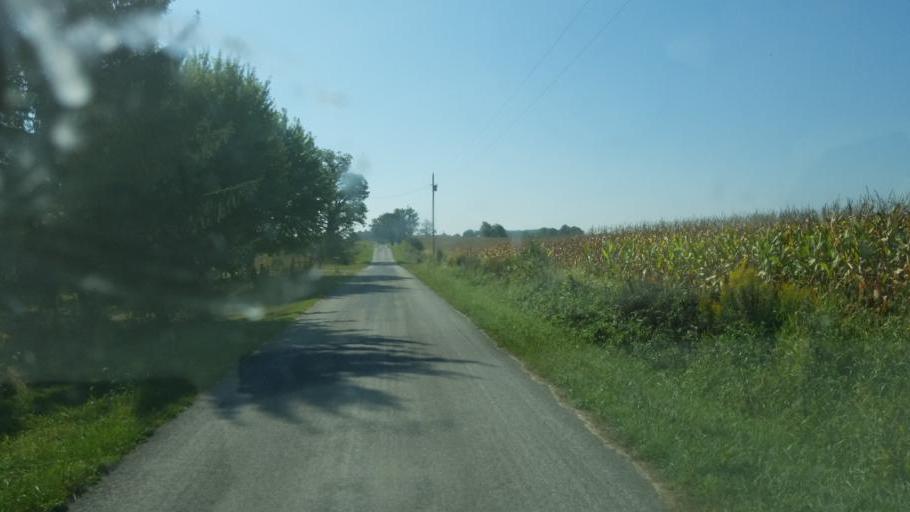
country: US
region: Ohio
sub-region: Union County
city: Richwood
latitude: 40.5135
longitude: -83.4077
